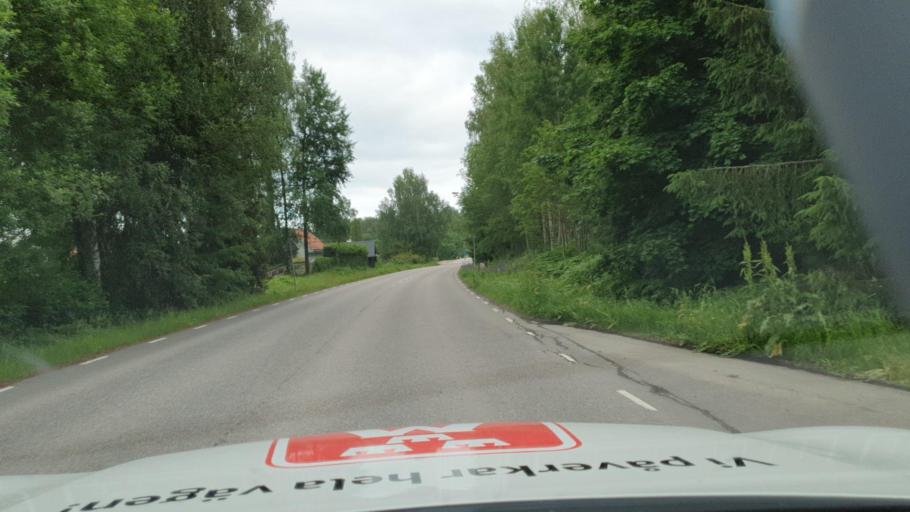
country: SE
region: Vaermland
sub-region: Karlstads Kommun
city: Karlstad
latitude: 59.4430
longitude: 13.4418
